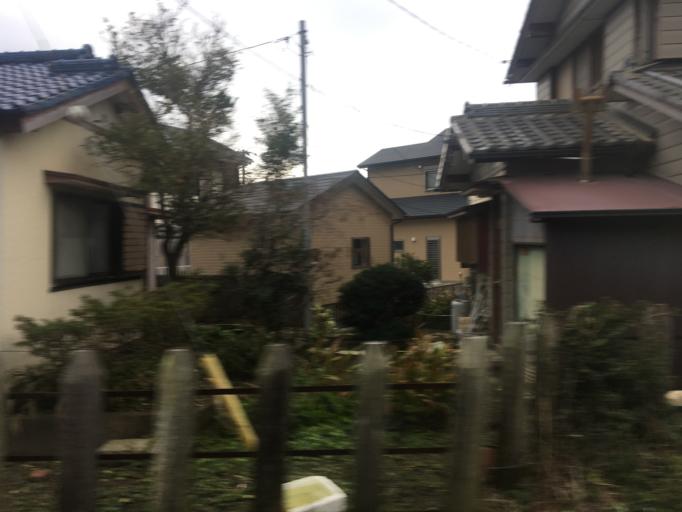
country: JP
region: Chiba
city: Kawaguchi
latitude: 35.0626
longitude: 140.0622
